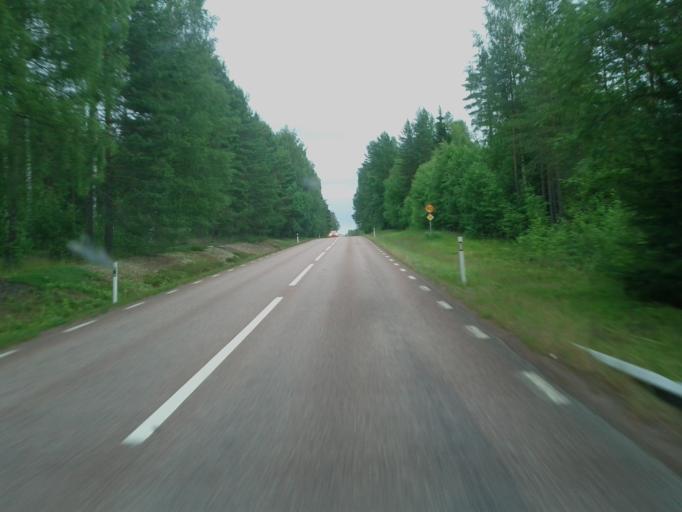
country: SE
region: Dalarna
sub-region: Mora Kommun
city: Mora
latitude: 61.0761
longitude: 14.3462
